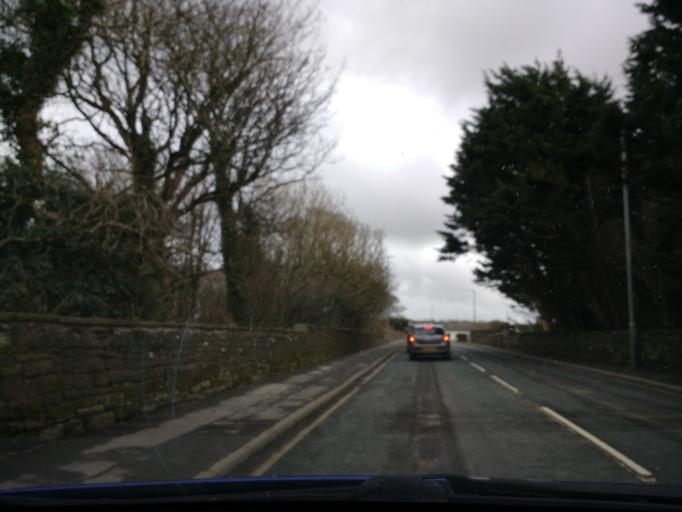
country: GB
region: England
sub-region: Cumbria
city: Maryport
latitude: 54.7134
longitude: -3.4909
